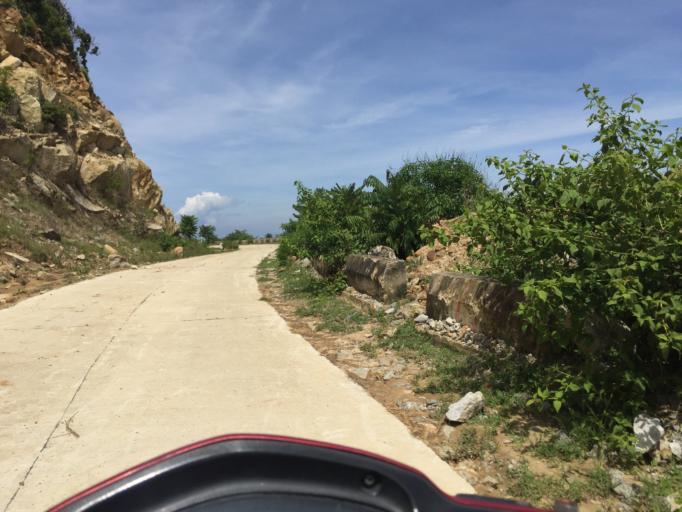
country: VN
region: Quang Nam
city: Hoi An
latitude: 15.9739
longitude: 108.5078
